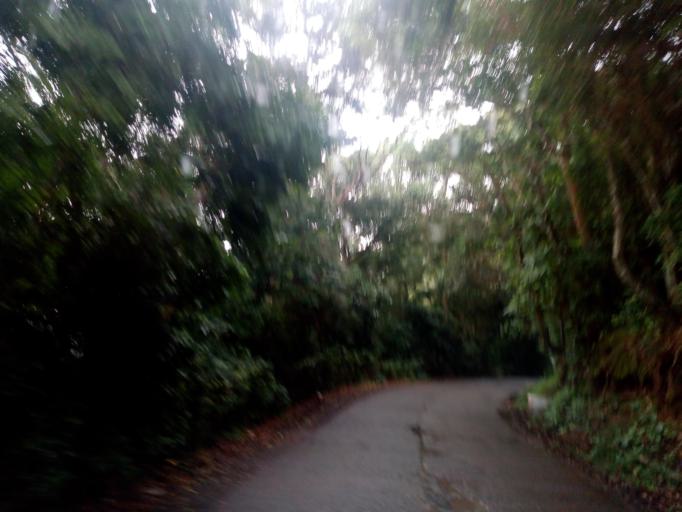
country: IN
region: Tamil Nadu
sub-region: Nilgiri
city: Wellington
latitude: 11.3501
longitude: 76.8297
